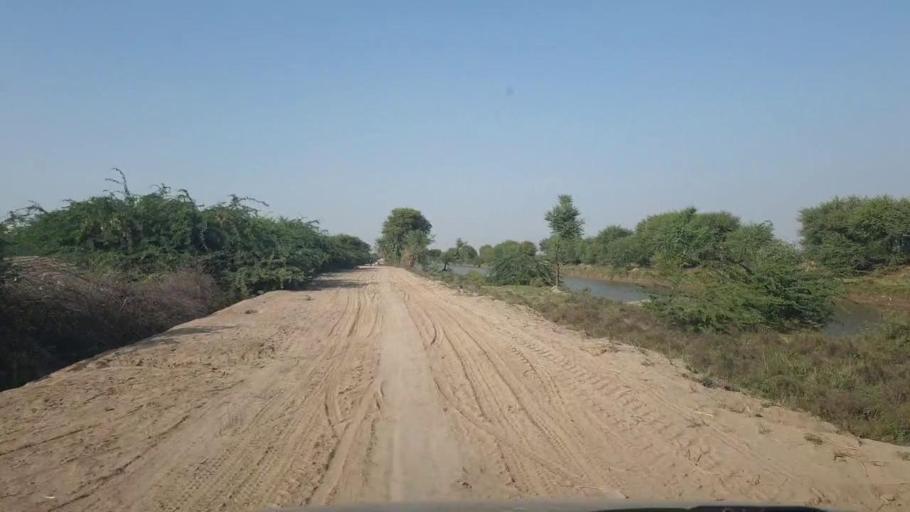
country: PK
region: Sindh
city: Badin
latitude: 24.6320
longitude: 68.8150
